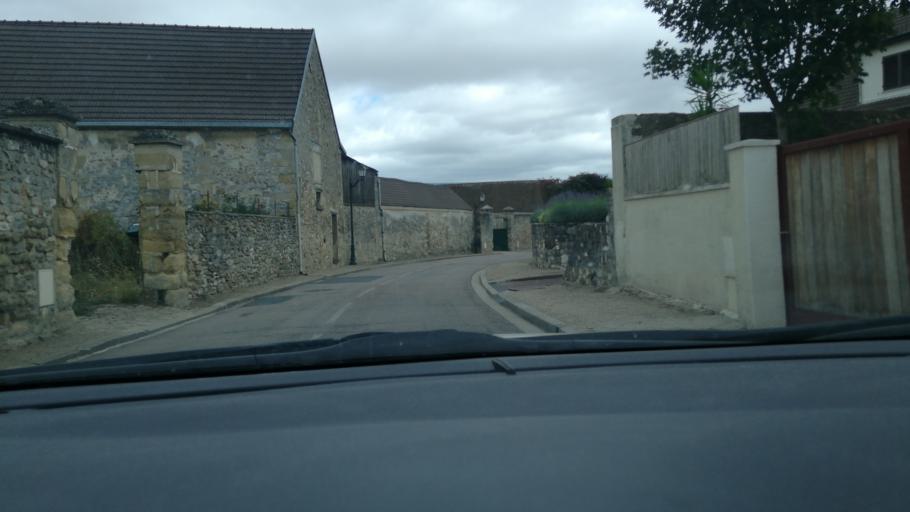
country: FR
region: Ile-de-France
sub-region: Departement du Val-d'Oise
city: Osny
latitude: 49.0907
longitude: 2.0697
